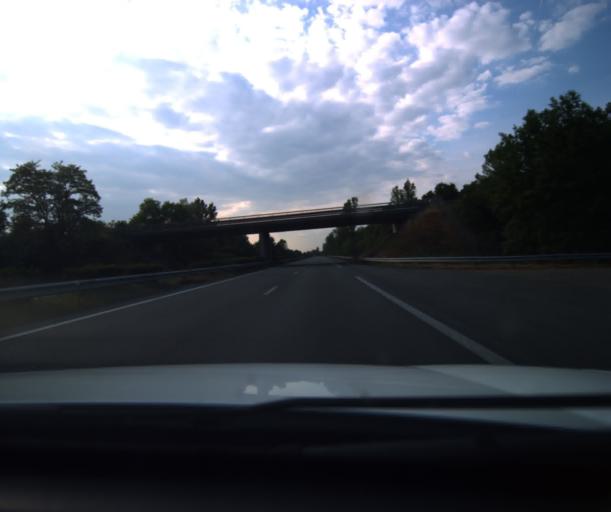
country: FR
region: Midi-Pyrenees
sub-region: Departement du Tarn-et-Garonne
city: Montech
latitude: 43.9695
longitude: 1.2688
